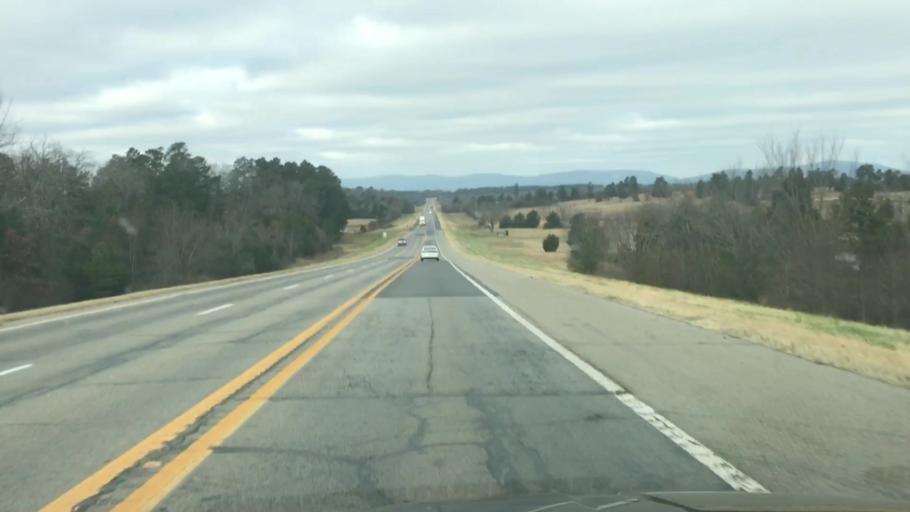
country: US
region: Arkansas
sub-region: Scott County
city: Waldron
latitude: 34.8678
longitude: -94.0784
